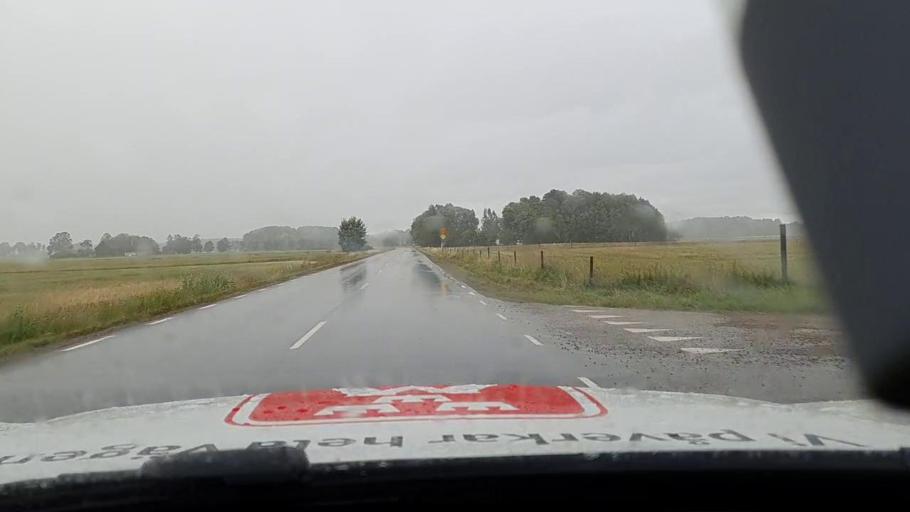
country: SE
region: Vaestra Goetaland
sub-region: Toreboda Kommun
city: Toereboda
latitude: 58.6669
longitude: 14.1313
